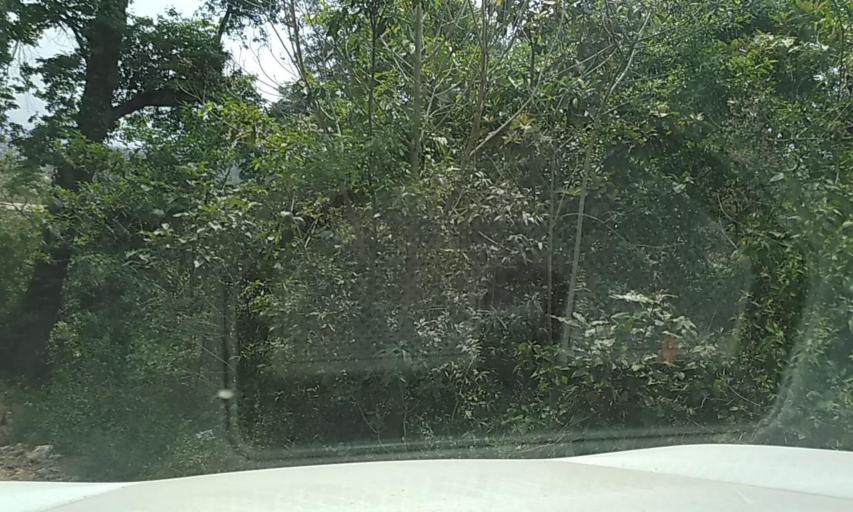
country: MX
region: Veracruz
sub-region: Jilotepec
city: El Pueblito (Garbanzal)
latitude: 19.5763
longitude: -96.8939
